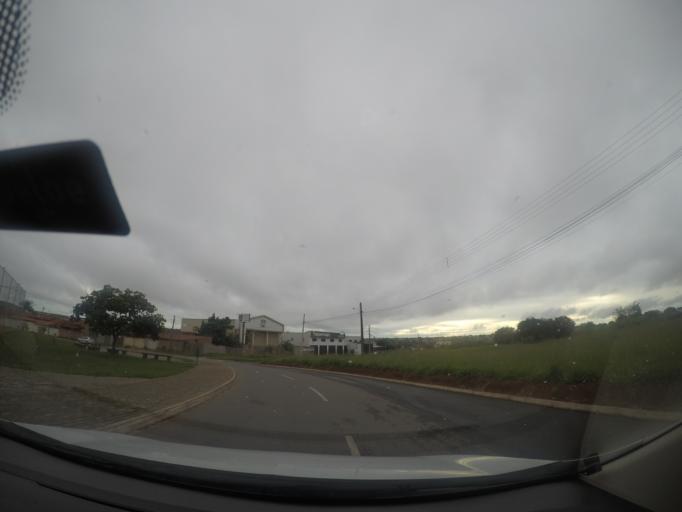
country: BR
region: Goias
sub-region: Goiania
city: Goiania
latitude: -16.7535
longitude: -49.3200
